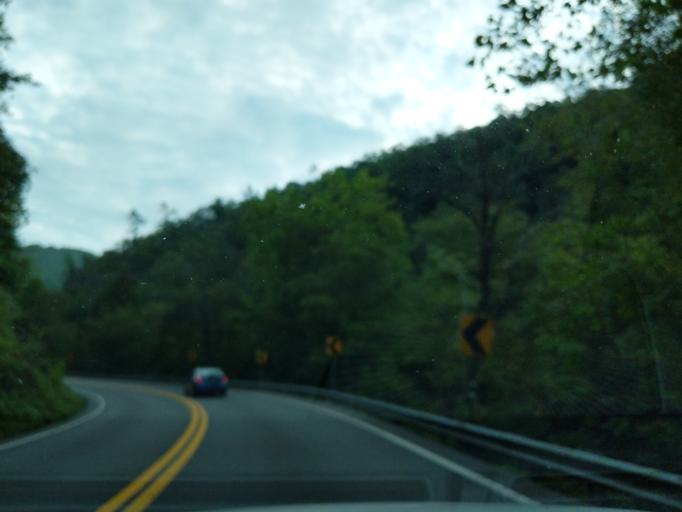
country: US
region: Tennessee
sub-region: Polk County
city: Benton
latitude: 35.0953
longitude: -84.5413
